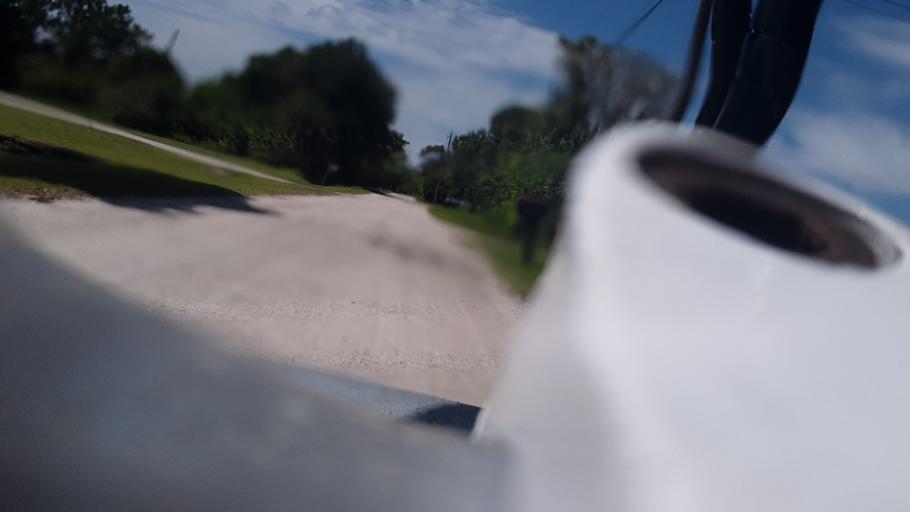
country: US
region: Florida
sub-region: Brevard County
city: Malabar
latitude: 27.9895
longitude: -80.6100
